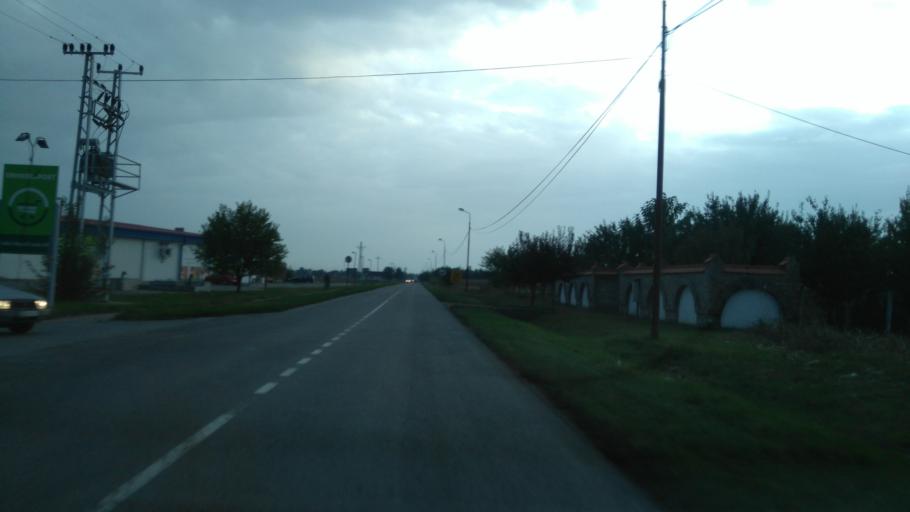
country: RS
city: Mol
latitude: 45.7826
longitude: 20.1278
